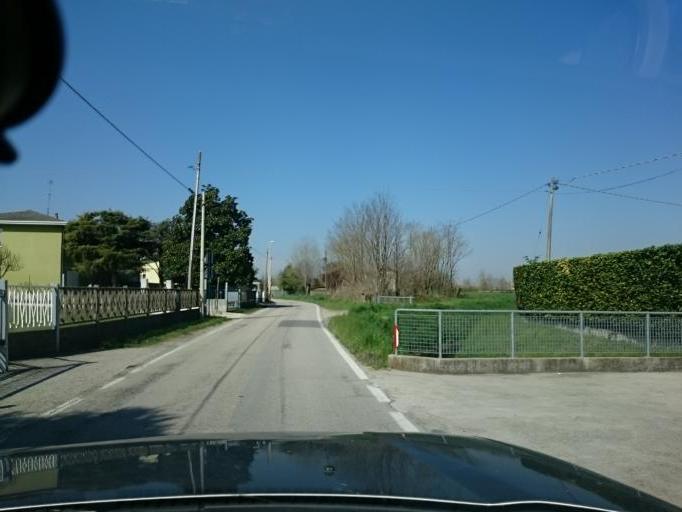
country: IT
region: Veneto
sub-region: Provincia di Padova
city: Albignasego
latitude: 45.3680
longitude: 11.8988
